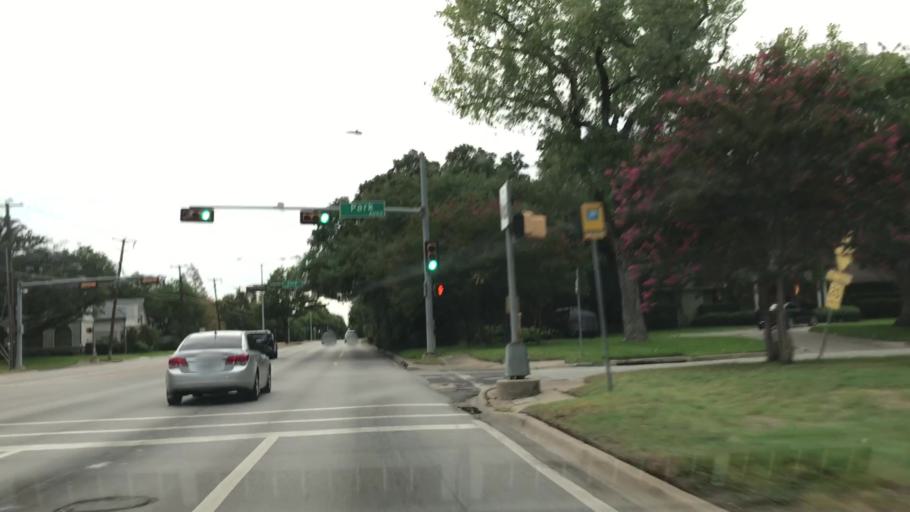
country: US
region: Texas
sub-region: Dallas County
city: University Park
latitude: 32.8733
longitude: -96.8039
